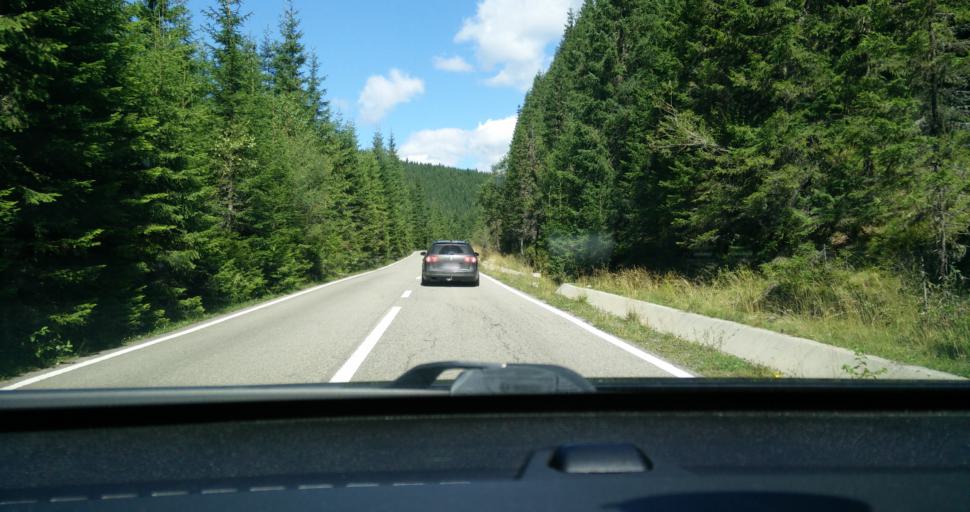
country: RO
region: Alba
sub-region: Comuna Sugag
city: Sugag
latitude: 45.5338
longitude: 23.6415
